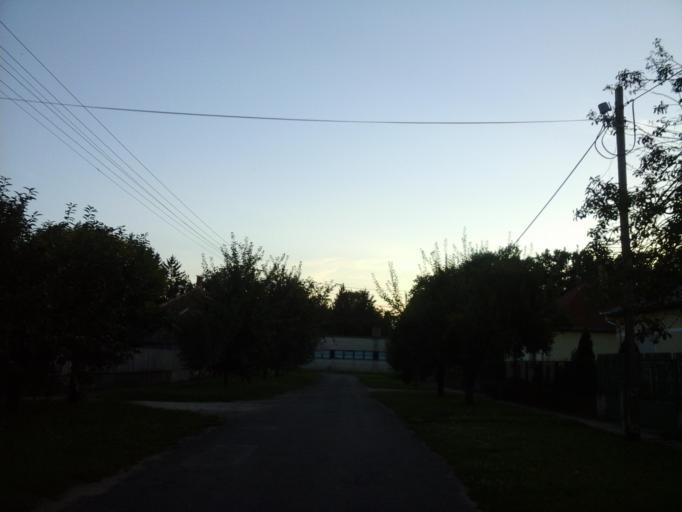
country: HU
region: Hajdu-Bihar
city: Hajduszoboszlo
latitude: 47.4610
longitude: 21.4129
